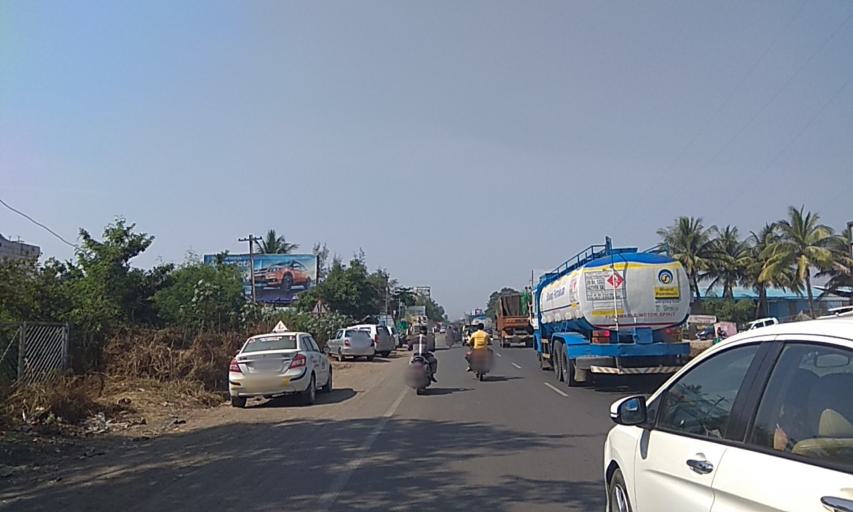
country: IN
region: Maharashtra
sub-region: Pune Division
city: Lohogaon
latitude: 18.4950
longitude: 73.9796
